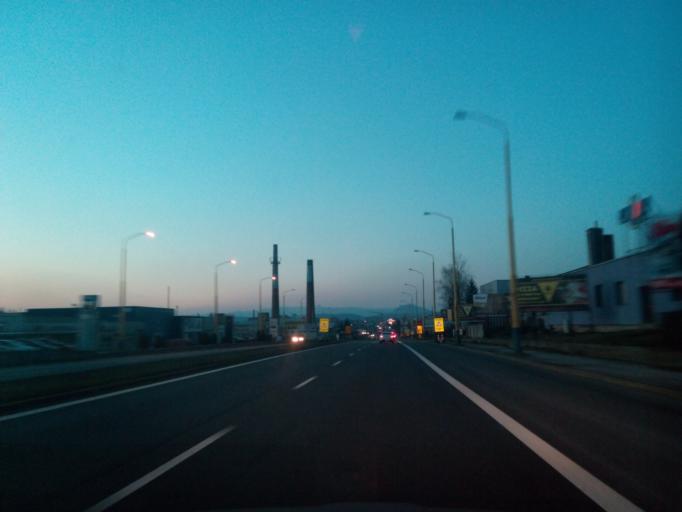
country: SK
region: Presovsky
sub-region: Okres Presov
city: Presov
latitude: 48.9648
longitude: 21.2553
